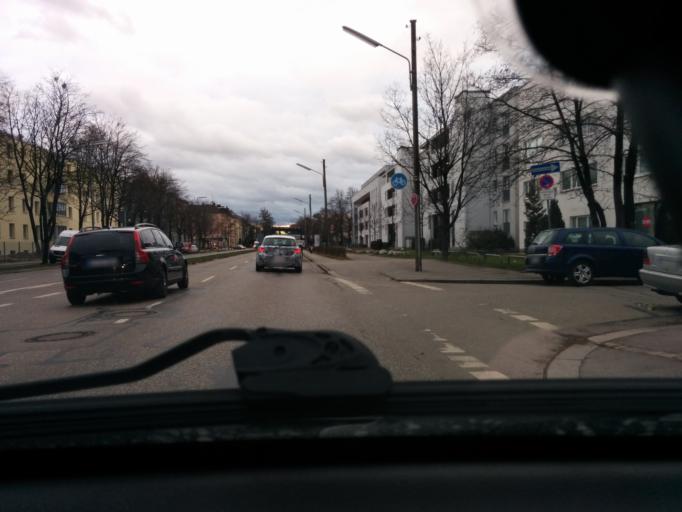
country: DE
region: Bavaria
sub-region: Upper Bavaria
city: Munich
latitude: 48.1863
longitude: 11.5661
